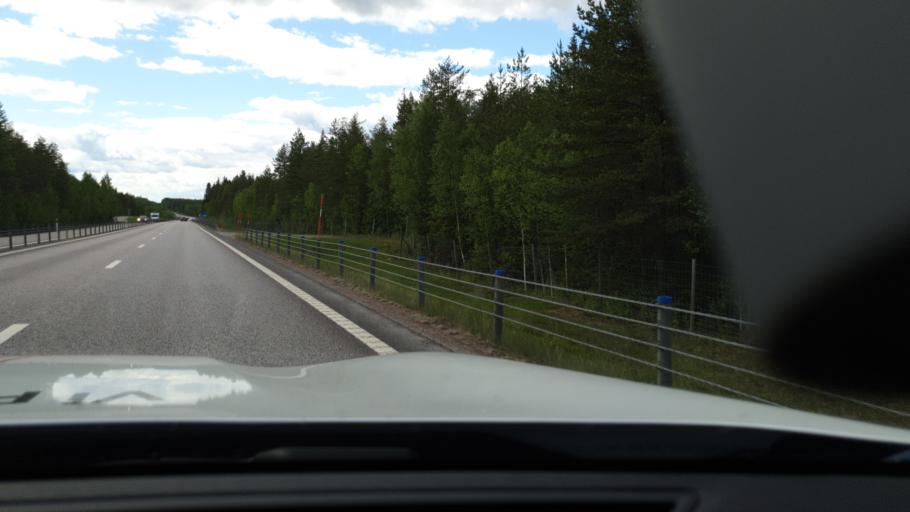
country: SE
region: Norrbotten
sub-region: Pitea Kommun
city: Rosvik
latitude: 65.4785
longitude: 21.7347
